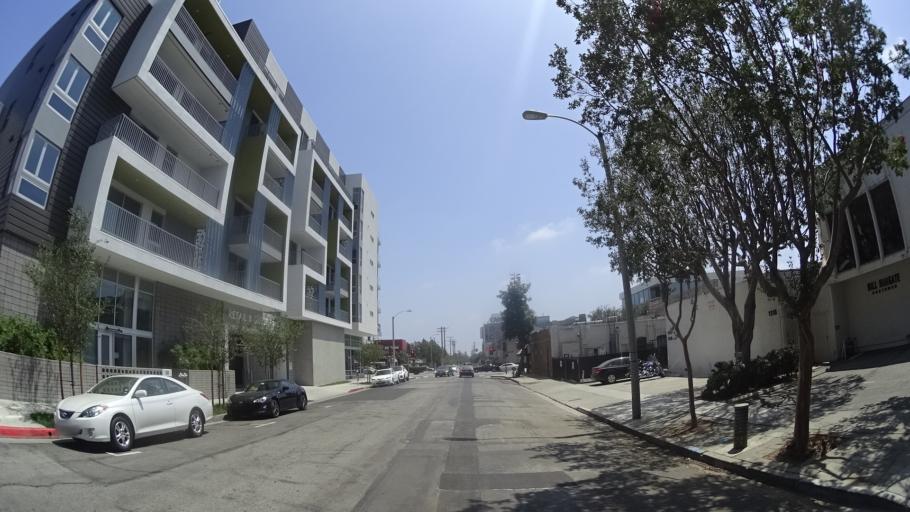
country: US
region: California
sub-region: Los Angeles County
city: West Hollywood
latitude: 34.0914
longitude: -118.3462
